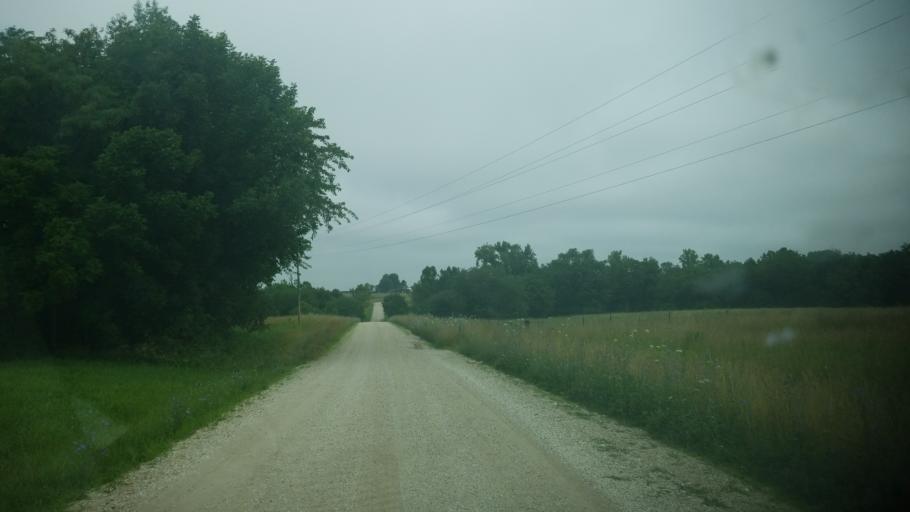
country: US
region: Missouri
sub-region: Pike County
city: Bowling Green
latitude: 39.3553
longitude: -91.2618
